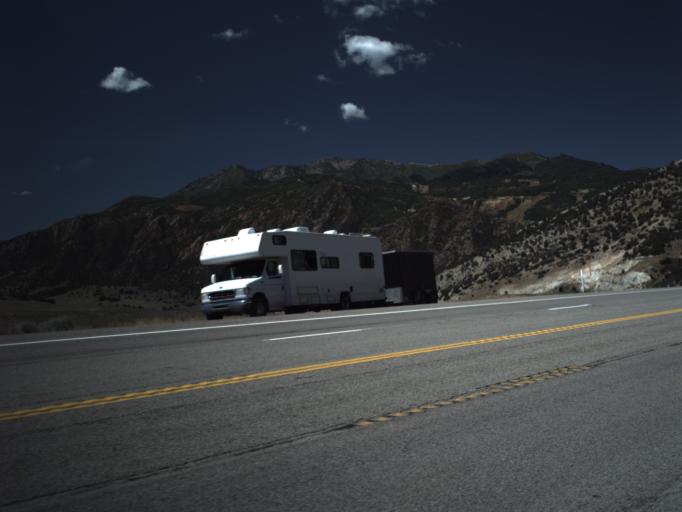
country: US
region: Utah
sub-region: Utah County
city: Mapleton
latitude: 39.9965
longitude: -111.4733
